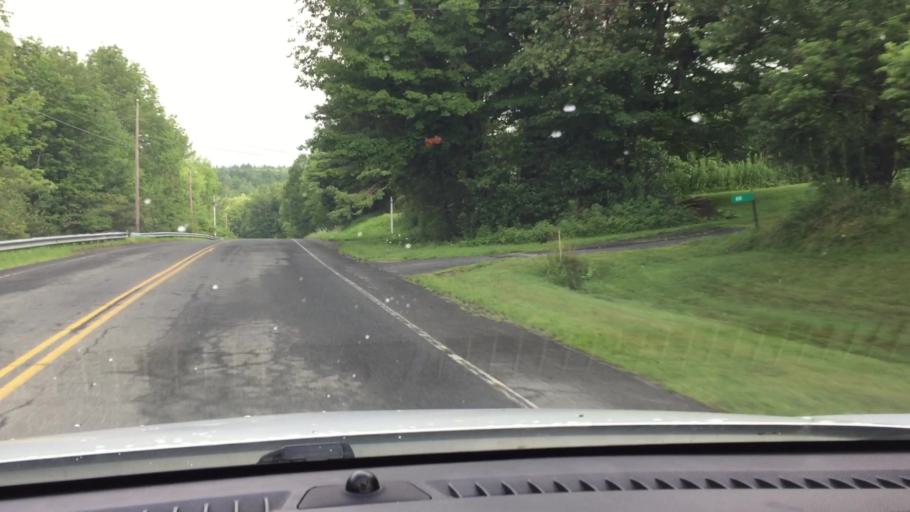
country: US
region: Massachusetts
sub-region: Berkshire County
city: Hinsdale
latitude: 42.4318
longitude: -73.0169
